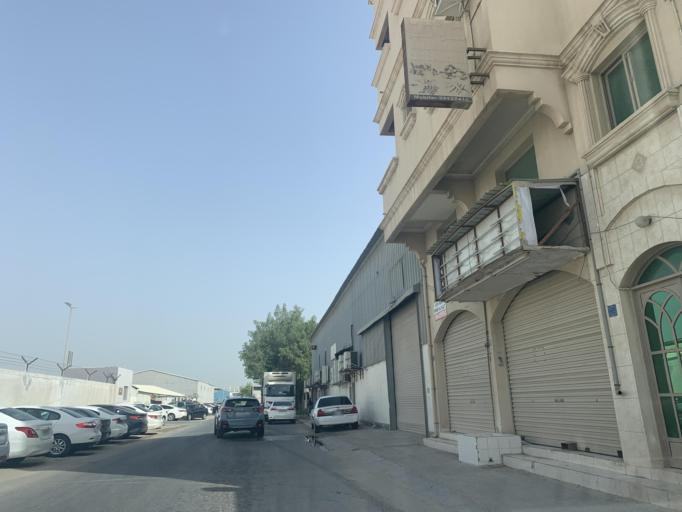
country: BH
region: Northern
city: Sitrah
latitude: 26.1520
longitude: 50.6197
